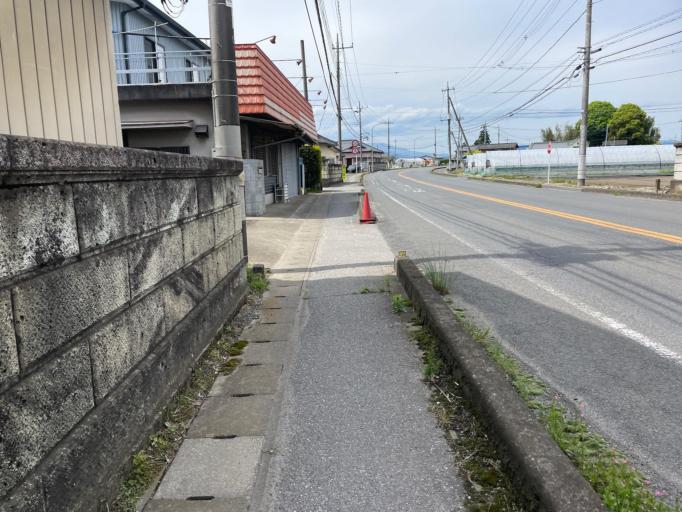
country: JP
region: Tochigi
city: Mibu
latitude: 36.4681
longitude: 139.7653
